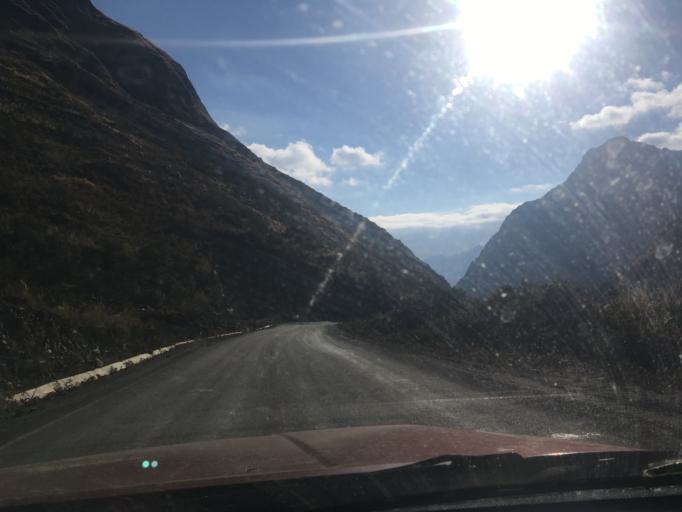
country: BO
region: La Paz
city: Quime
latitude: -17.0022
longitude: -67.2679
